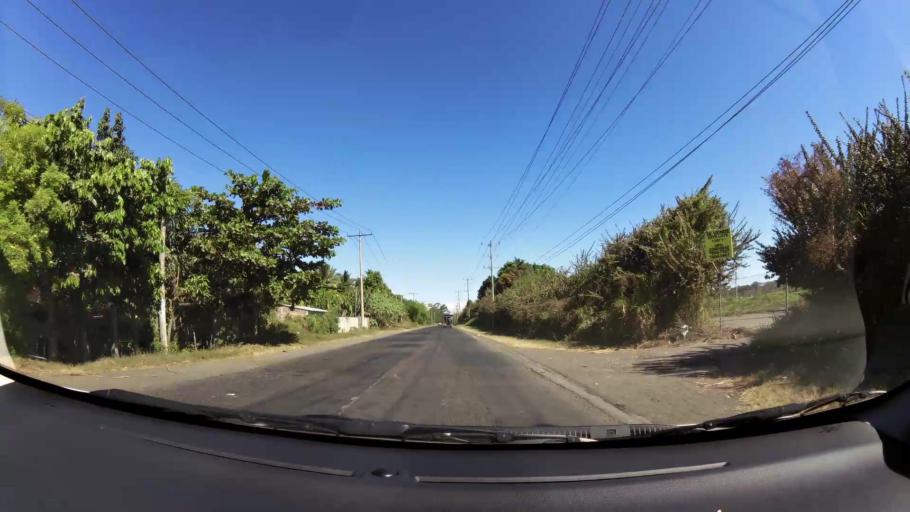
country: SV
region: La Libertad
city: San Juan Opico
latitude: 13.8060
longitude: -89.3586
